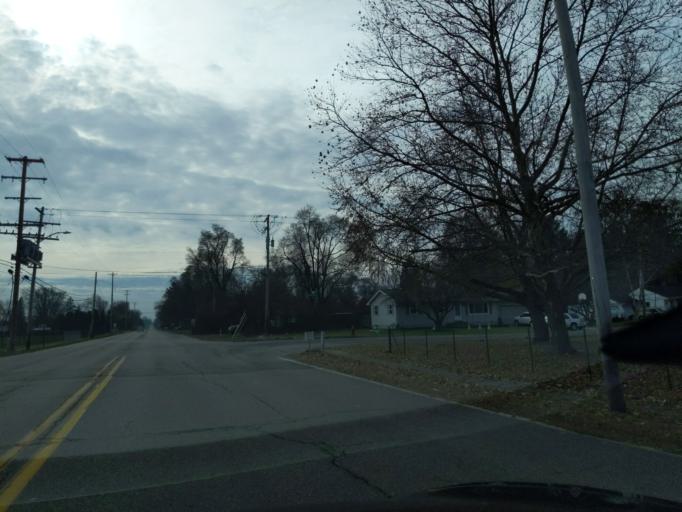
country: US
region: Michigan
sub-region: Ingham County
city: Holt
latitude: 42.6332
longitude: -84.5234
